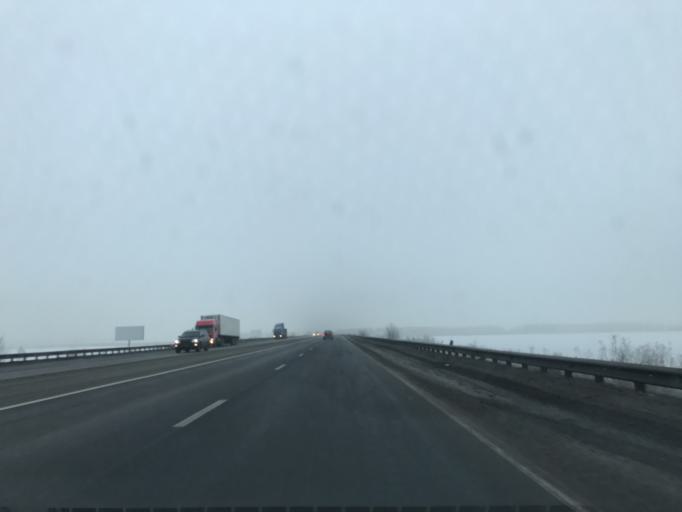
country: RU
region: Rostov
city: Grushevskaya
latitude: 47.4530
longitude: 39.9740
